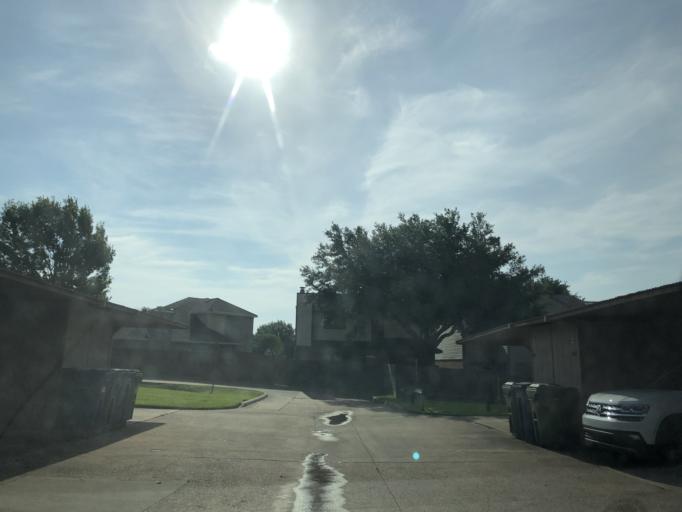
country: US
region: Texas
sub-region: Dallas County
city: Sunnyvale
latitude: 32.8412
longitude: -96.6115
